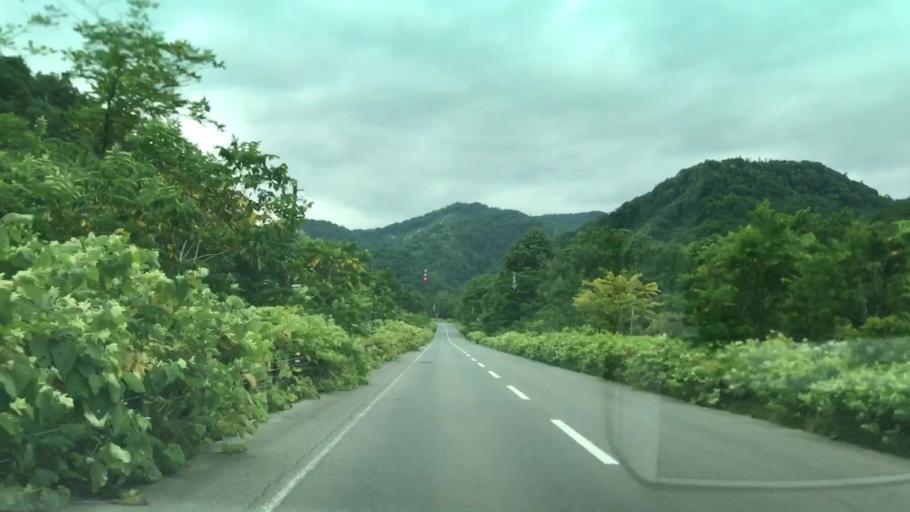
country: JP
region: Hokkaido
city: Yoichi
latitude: 43.0184
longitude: 140.8678
